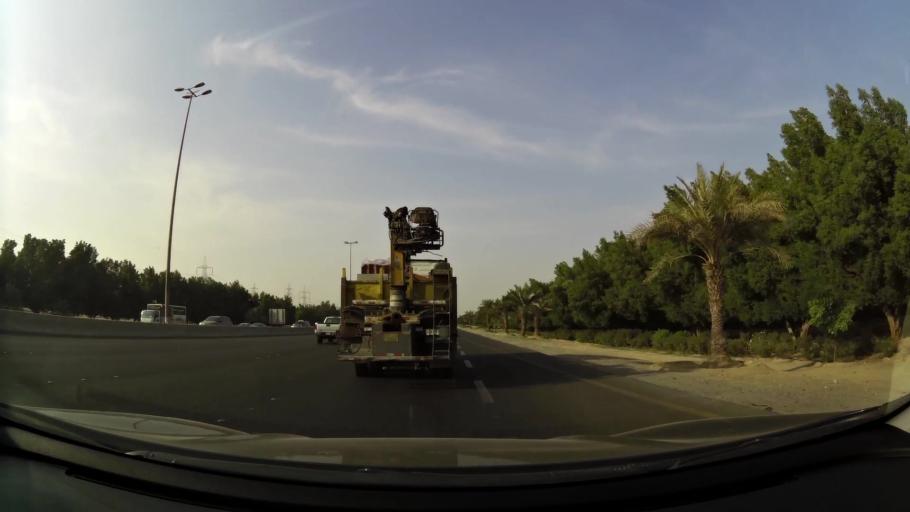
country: KW
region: Mubarak al Kabir
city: Mubarak al Kabir
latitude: 29.1955
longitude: 48.0630
